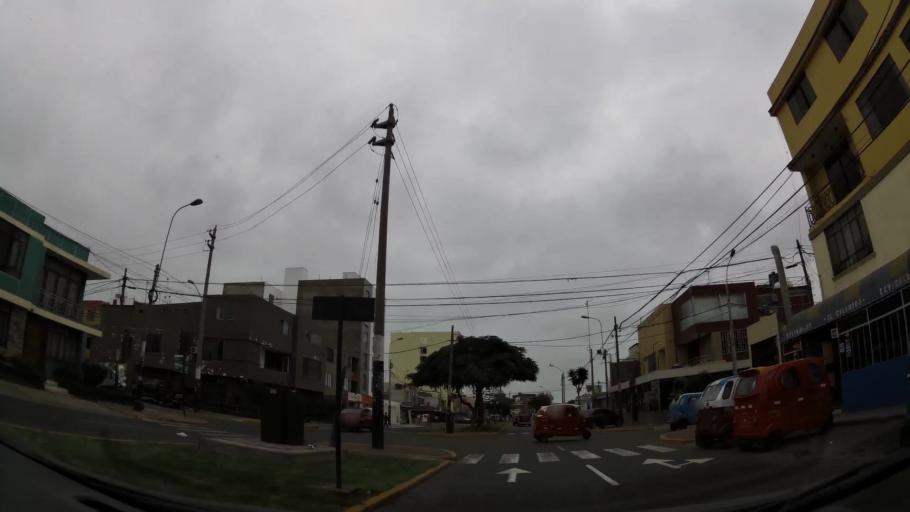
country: PE
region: Callao
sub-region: Callao
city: Callao
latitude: -12.0559
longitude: -77.0956
